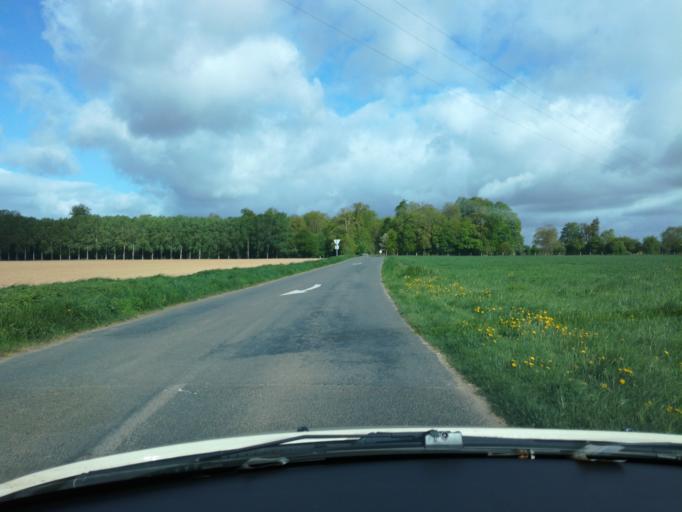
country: FR
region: Picardie
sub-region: Departement de la Somme
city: Hornoy-le-Bourg
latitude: 49.8437
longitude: 1.9116
